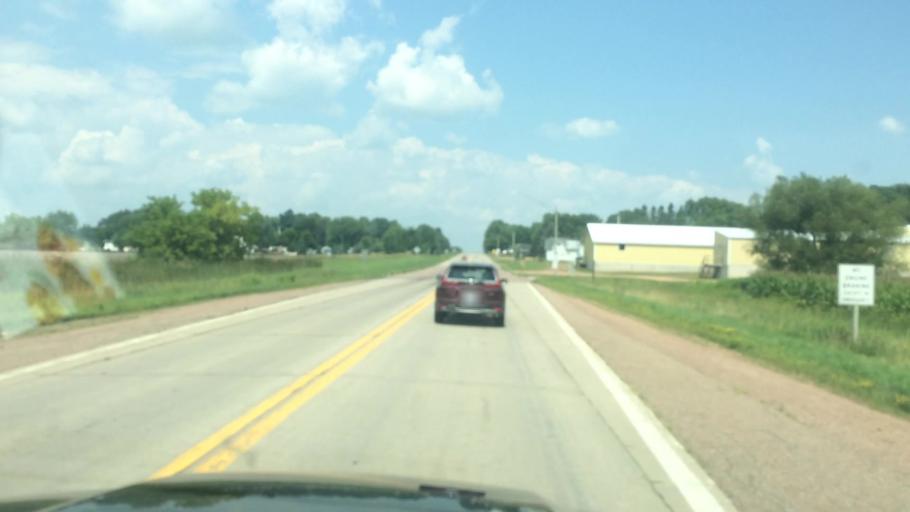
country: US
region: Wisconsin
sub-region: Clark County
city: Colby
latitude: 44.8432
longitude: -90.3159
